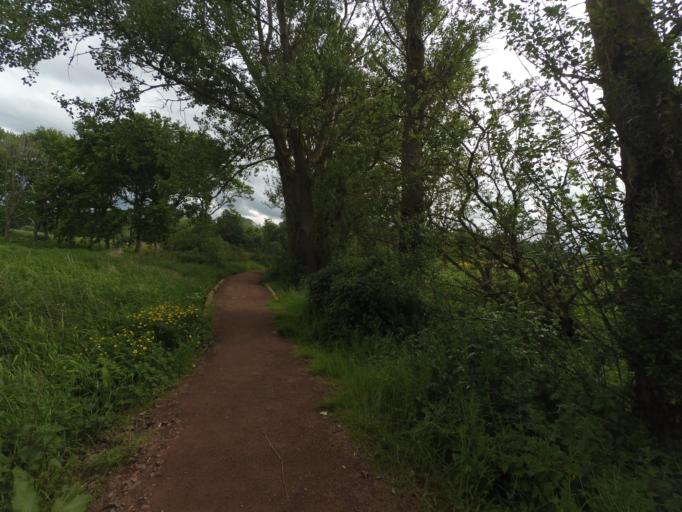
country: GB
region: Scotland
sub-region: East Lothian
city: Ormiston
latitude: 55.9127
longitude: -2.9223
